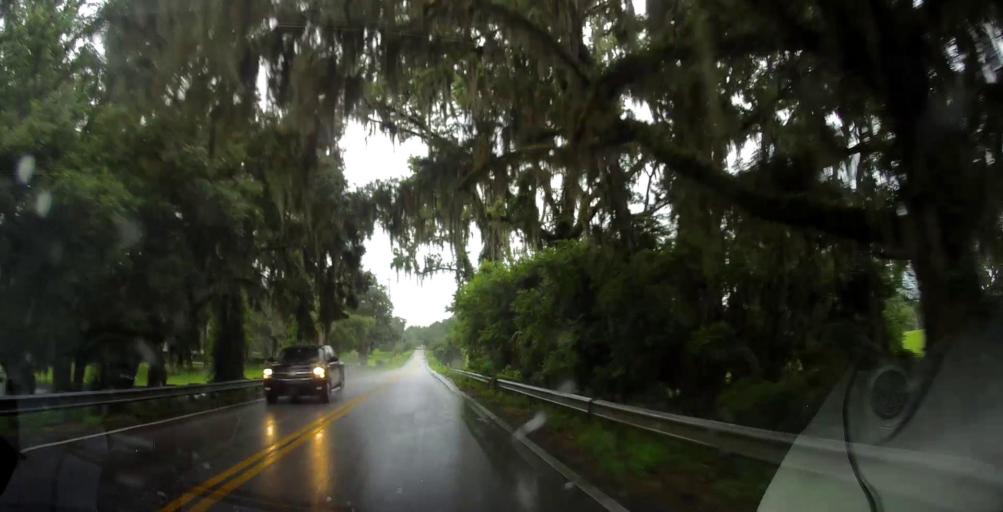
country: US
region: Florida
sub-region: Marion County
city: Citra
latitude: 29.3500
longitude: -82.2247
